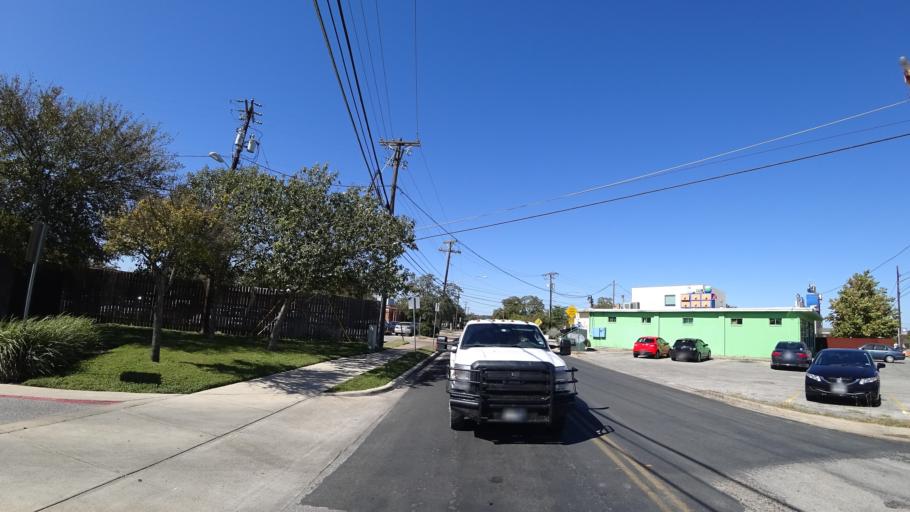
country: US
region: Texas
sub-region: Travis County
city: Austin
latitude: 30.3199
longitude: -97.7394
